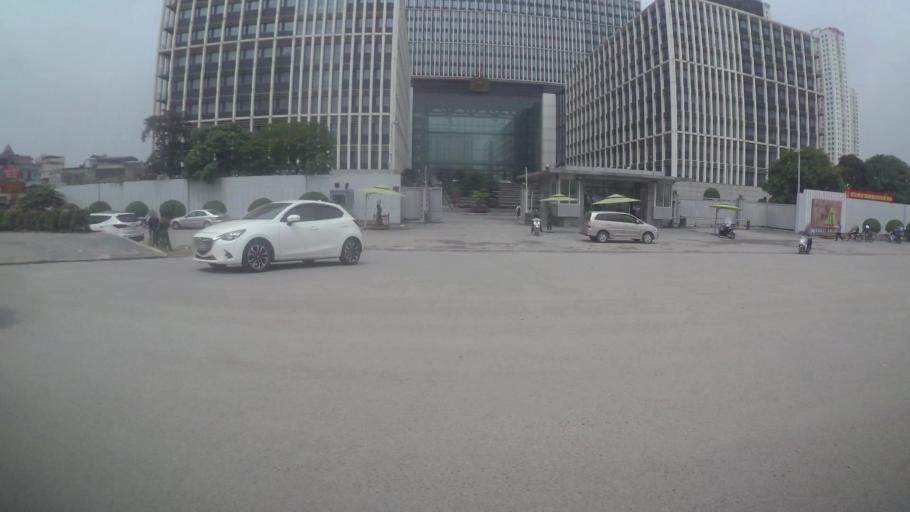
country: VN
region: Ha Noi
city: Cau Dien
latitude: 21.0484
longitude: 105.7813
